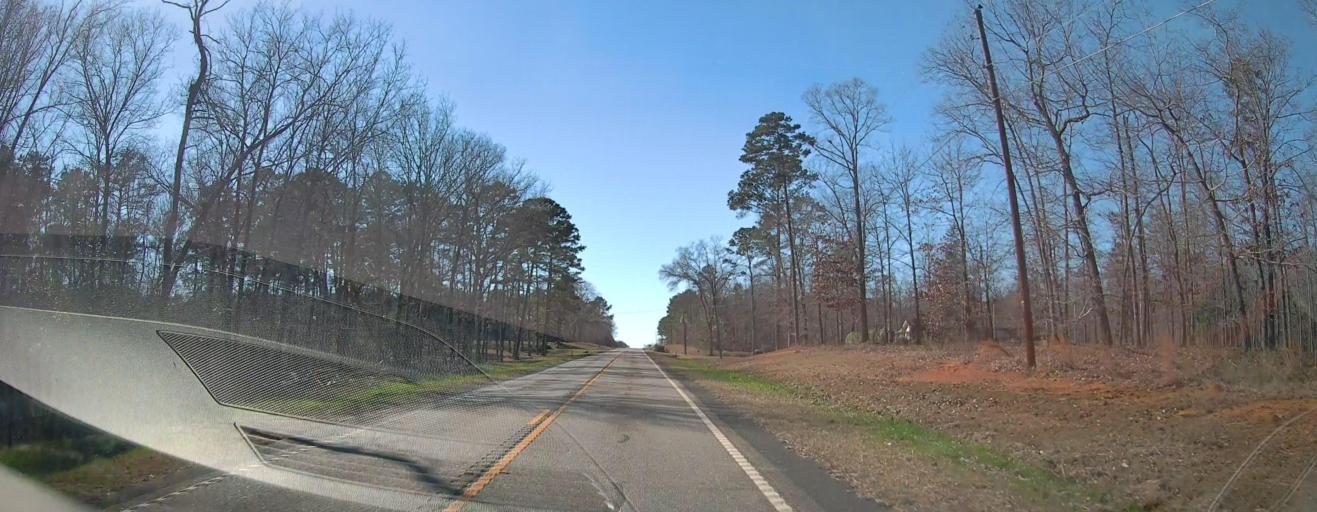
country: US
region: Georgia
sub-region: Schley County
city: Ellaville
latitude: 32.1819
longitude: -84.2553
